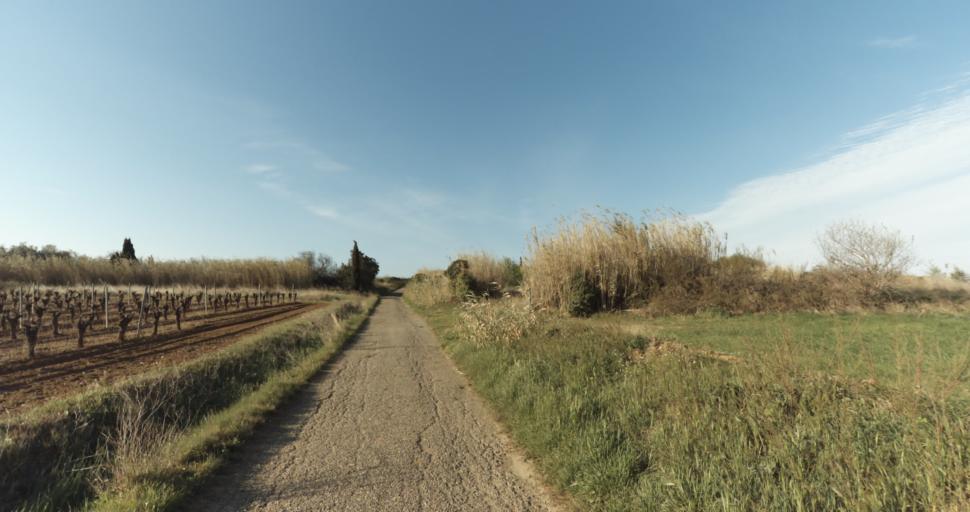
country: FR
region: Languedoc-Roussillon
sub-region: Departement de l'Herault
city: Marseillan
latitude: 43.3647
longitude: 3.5125
